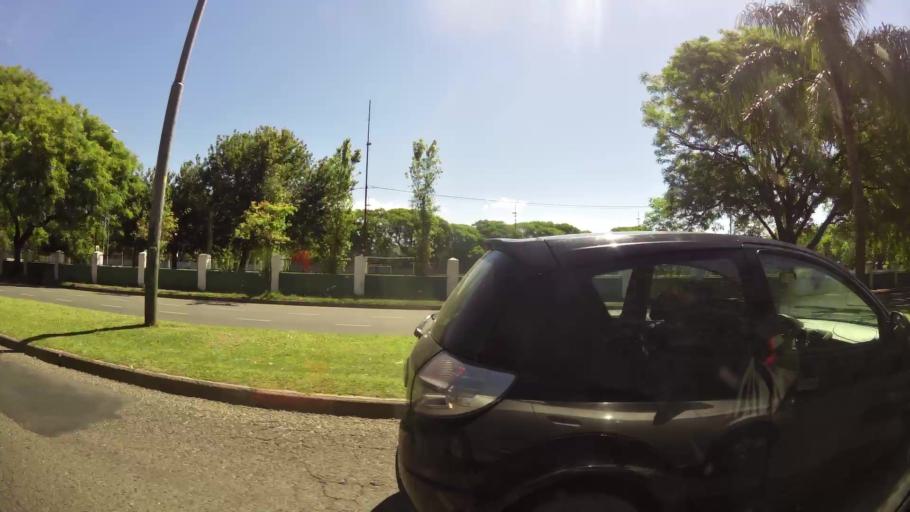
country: AR
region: Santa Fe
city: Santa Fe de la Vera Cruz
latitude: -31.6267
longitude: -60.6790
